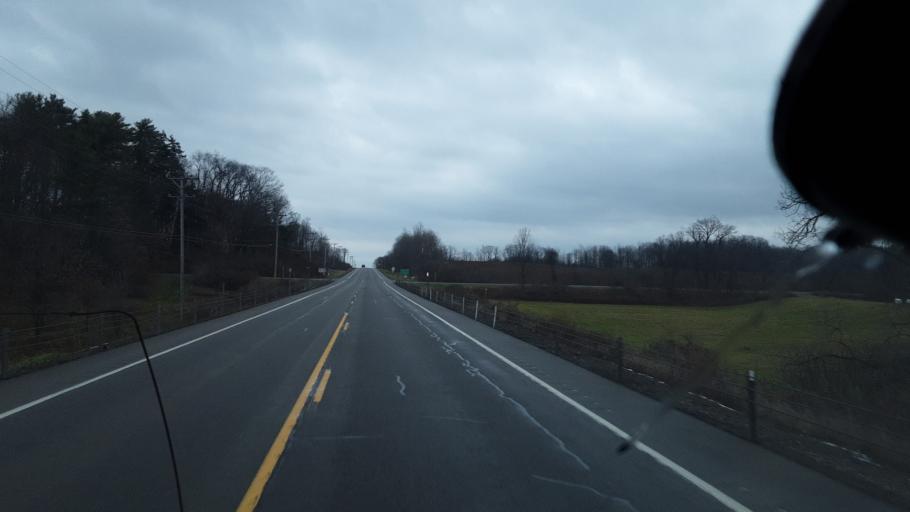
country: US
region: New York
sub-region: Allegany County
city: Houghton
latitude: 42.3913
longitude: -78.1930
